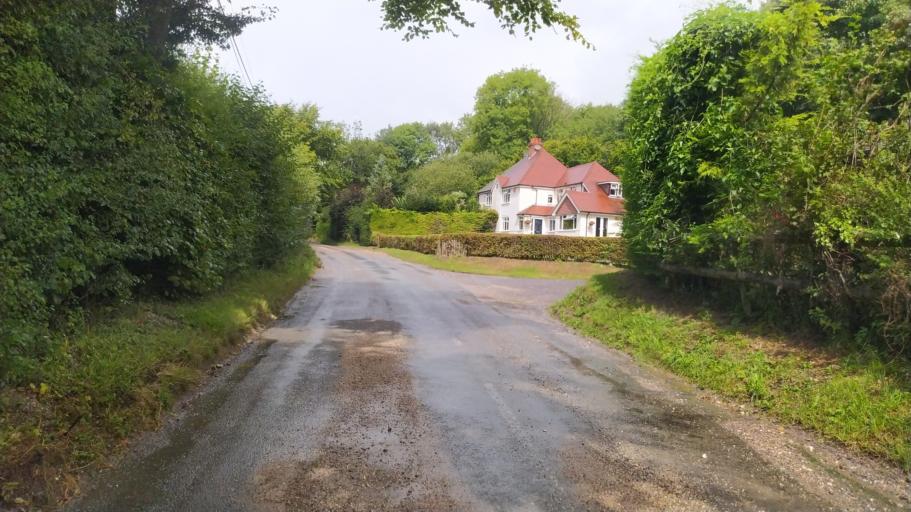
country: GB
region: England
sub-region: Hampshire
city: Swanmore
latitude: 51.0078
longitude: -1.1298
